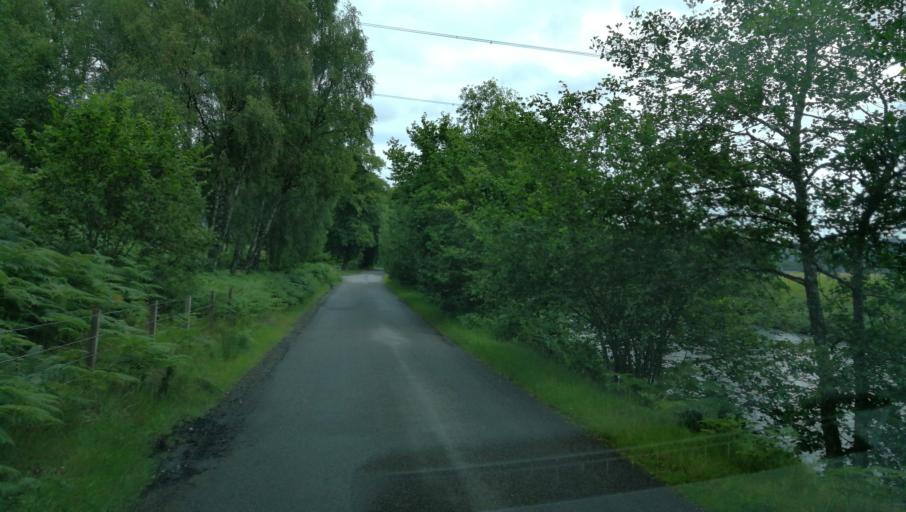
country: GB
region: Scotland
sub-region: Highland
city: Beauly
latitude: 57.3287
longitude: -4.7924
